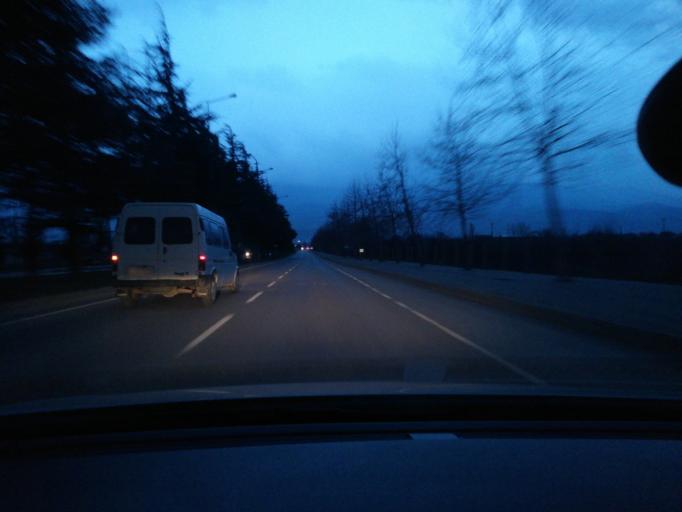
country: TR
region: Bolu
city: Bolu
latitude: 40.7111
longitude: 31.6159
